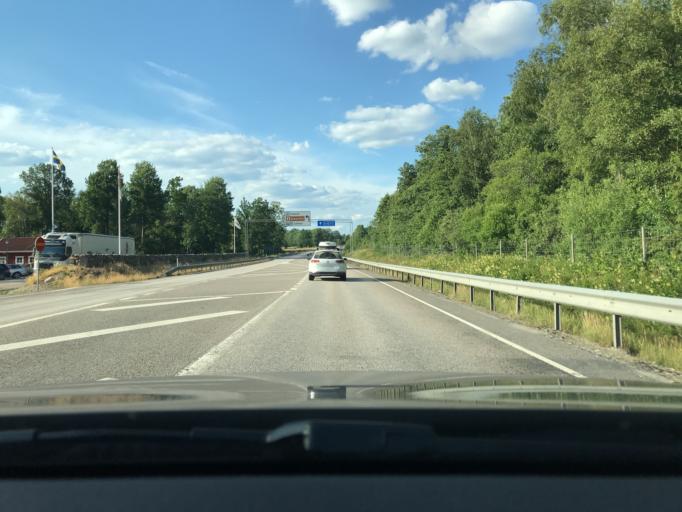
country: SE
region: Kronoberg
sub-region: Vaxjo Kommun
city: Rottne
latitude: 56.9772
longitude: 14.9816
